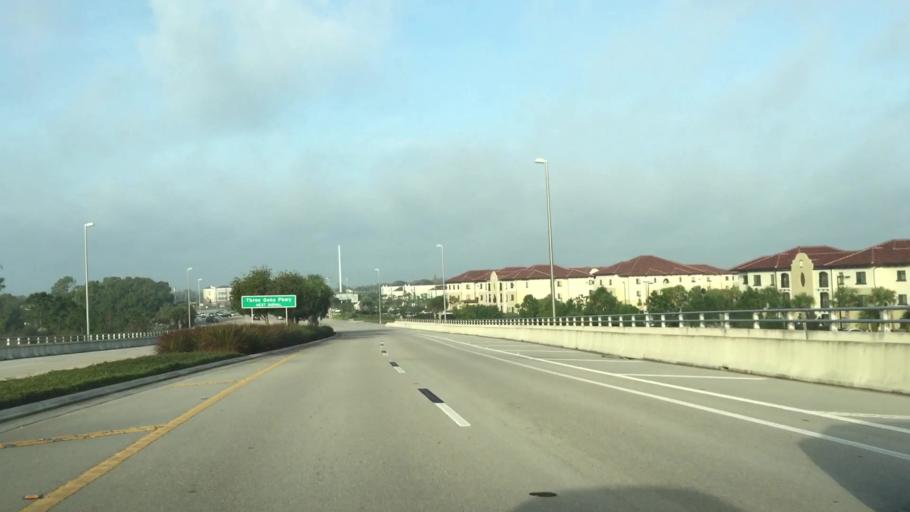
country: US
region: Florida
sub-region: Lee County
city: Three Oaks
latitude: 26.4491
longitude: -81.7857
